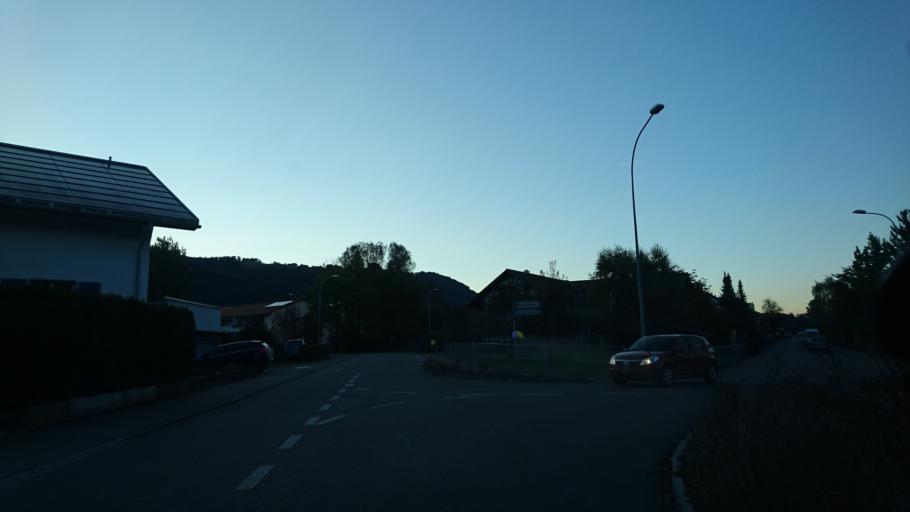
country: CH
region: Bern
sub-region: Bern-Mittelland District
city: Munsingen
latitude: 46.8744
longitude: 7.5505
